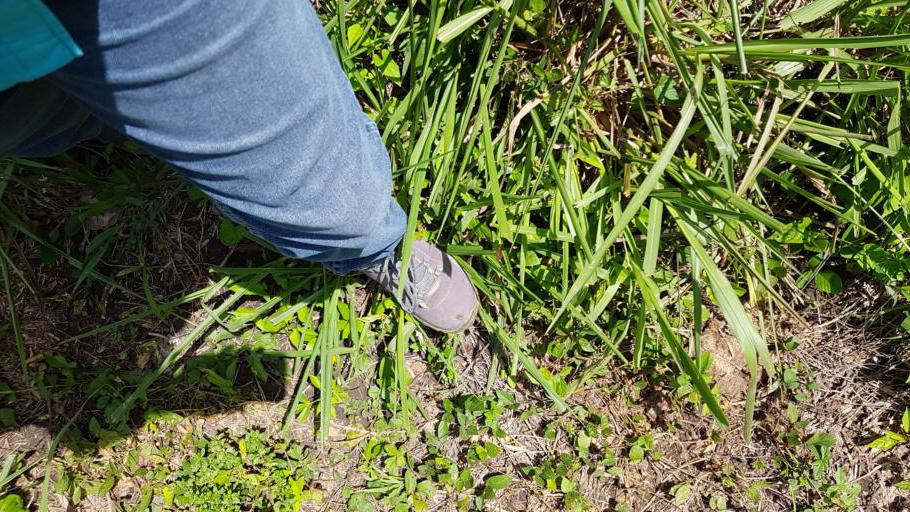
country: MX
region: Chiapas
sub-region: Catazaja
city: Catazaja
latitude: 17.7085
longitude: -92.0306
